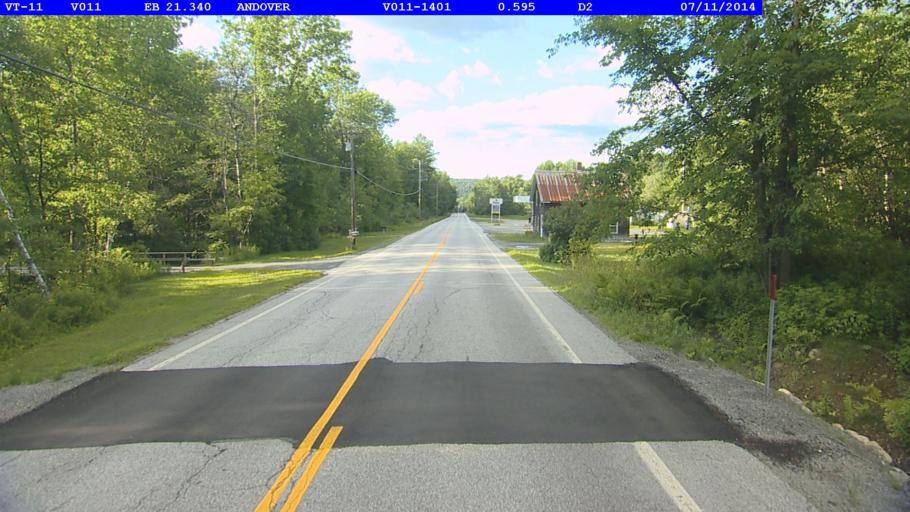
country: US
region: Vermont
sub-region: Windsor County
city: Chester
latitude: 43.2410
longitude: -72.7245
